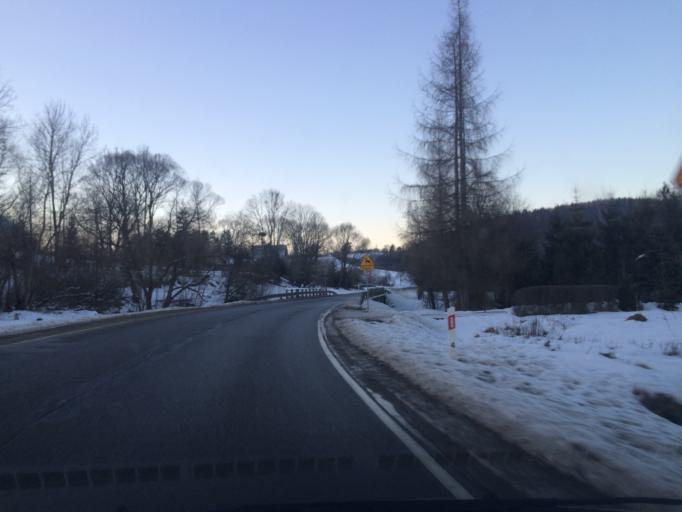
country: PL
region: Subcarpathian Voivodeship
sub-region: Powiat bieszczadzki
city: Czarna
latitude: 49.3834
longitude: 22.6374
